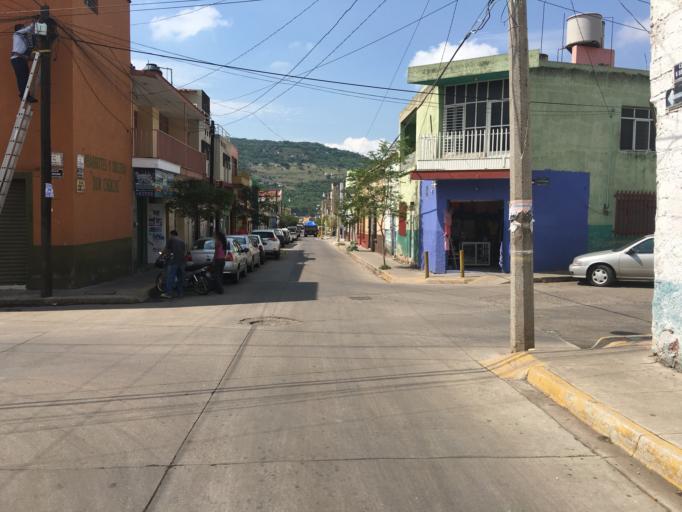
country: MX
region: Jalisco
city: Atotonilco el Alto
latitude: 20.5500
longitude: -102.5110
